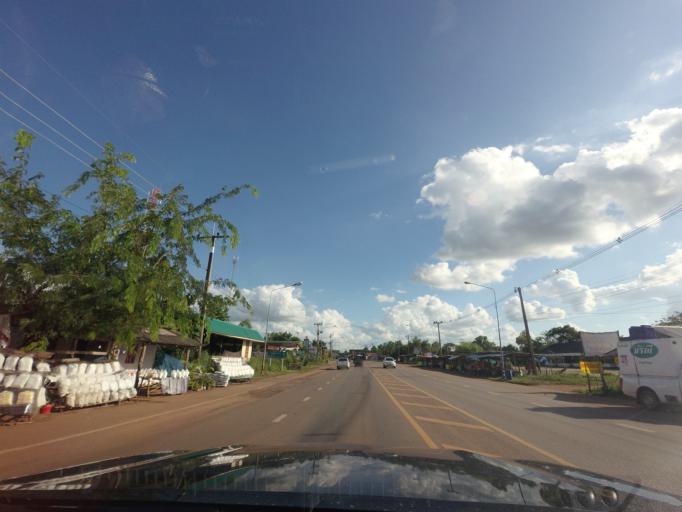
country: TH
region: Changwat Udon Thani
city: Ban Dung
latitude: 17.7117
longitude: 103.2502
